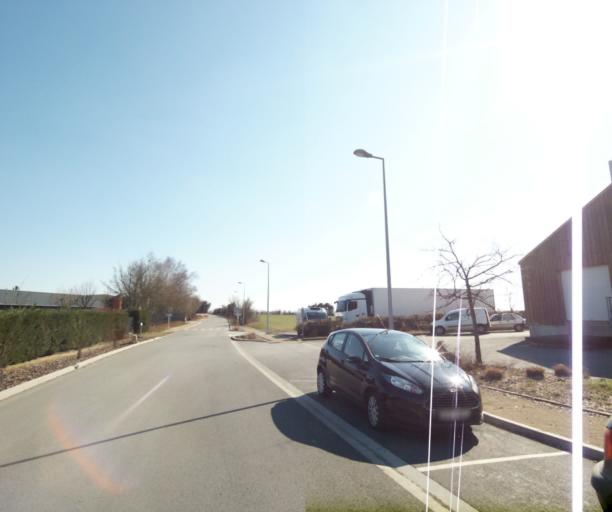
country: FR
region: Poitou-Charentes
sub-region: Departement des Deux-Sevres
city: Chauray
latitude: 46.3374
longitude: -0.3970
